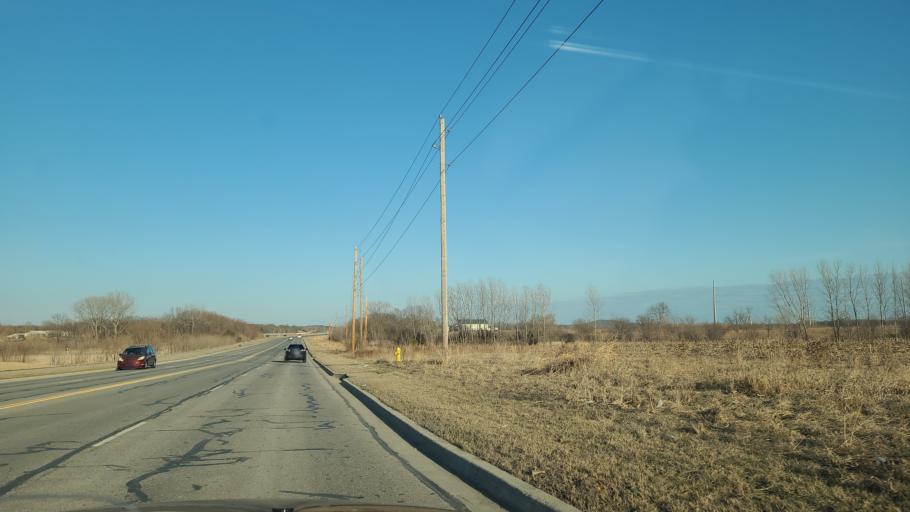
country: US
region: Kansas
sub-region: Douglas County
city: Lawrence
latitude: 38.9281
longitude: -95.2501
